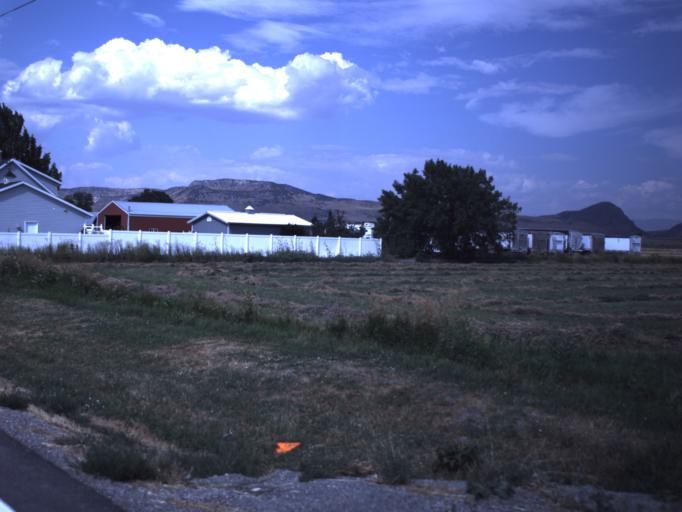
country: US
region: Utah
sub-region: Box Elder County
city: Garland
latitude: 41.8023
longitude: -112.1158
